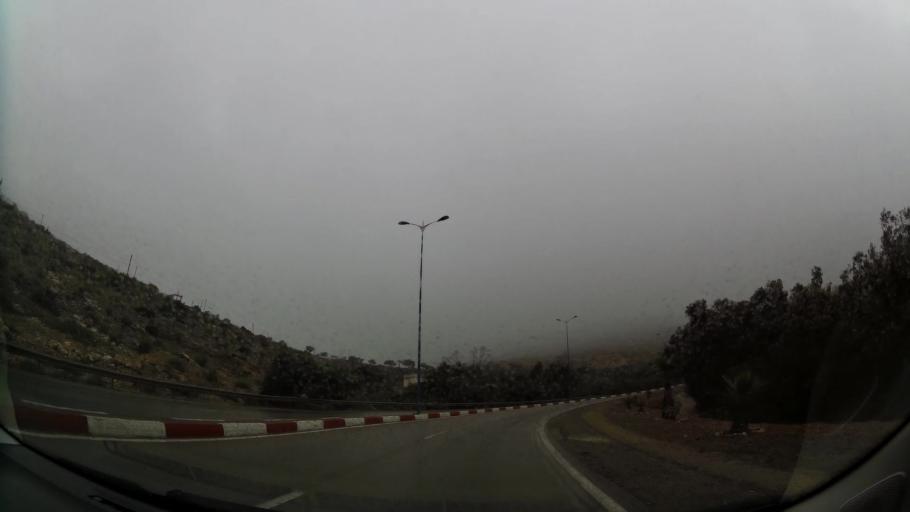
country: MA
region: Taza-Al Hoceima-Taounate
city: Al Hoceima
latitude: 35.2187
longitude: -3.9225
